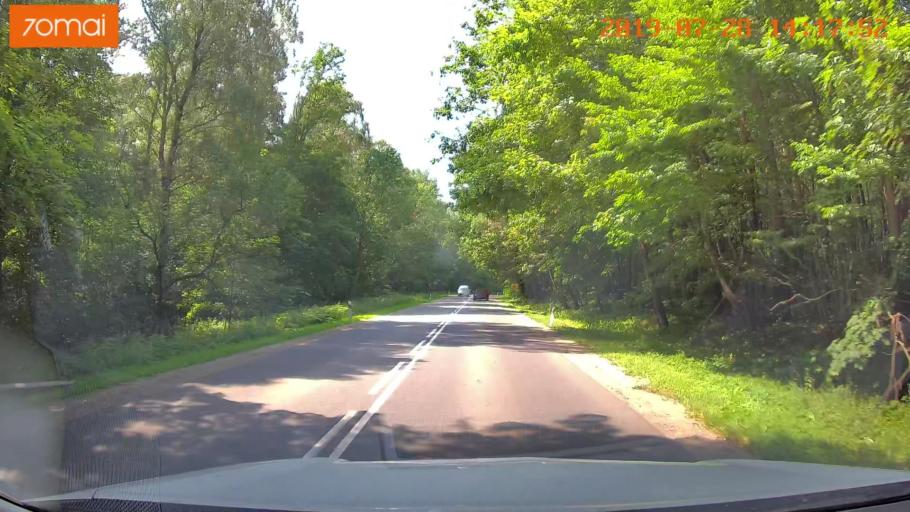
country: RU
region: Kaliningrad
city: Volochayevskoye
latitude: 54.8155
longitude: 20.2481
